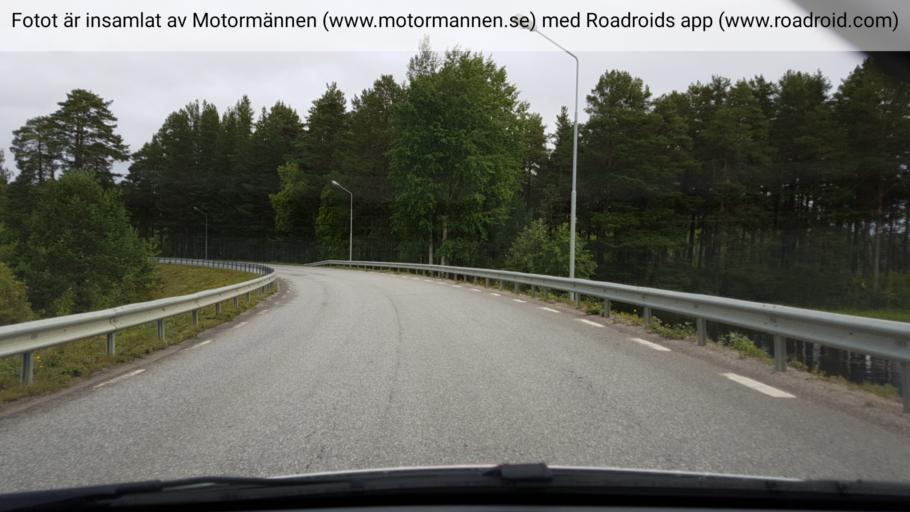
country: SE
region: Vaesterbotten
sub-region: Dorotea Kommun
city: Dorotea
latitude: 63.8030
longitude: 16.4125
